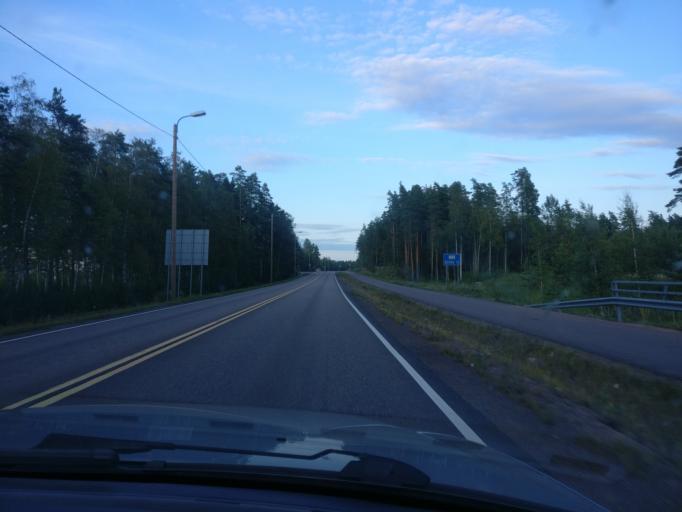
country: FI
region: Kymenlaakso
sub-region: Kotka-Hamina
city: Broby
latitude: 60.4957
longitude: 26.7431
